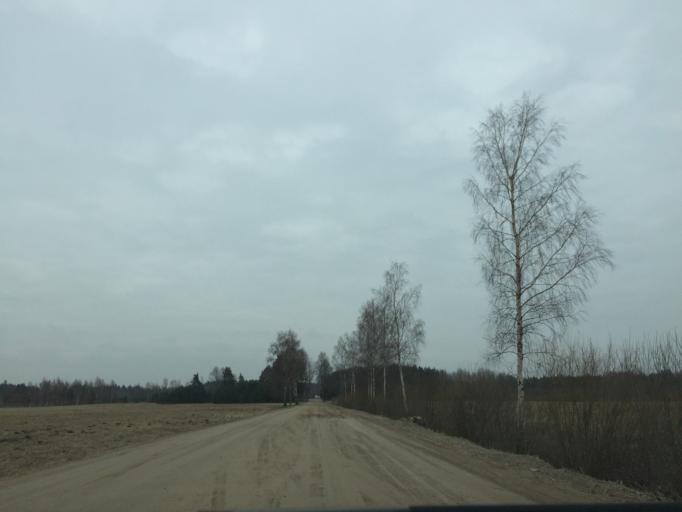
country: LV
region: Kekava
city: Kekava
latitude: 56.8022
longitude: 24.1652
